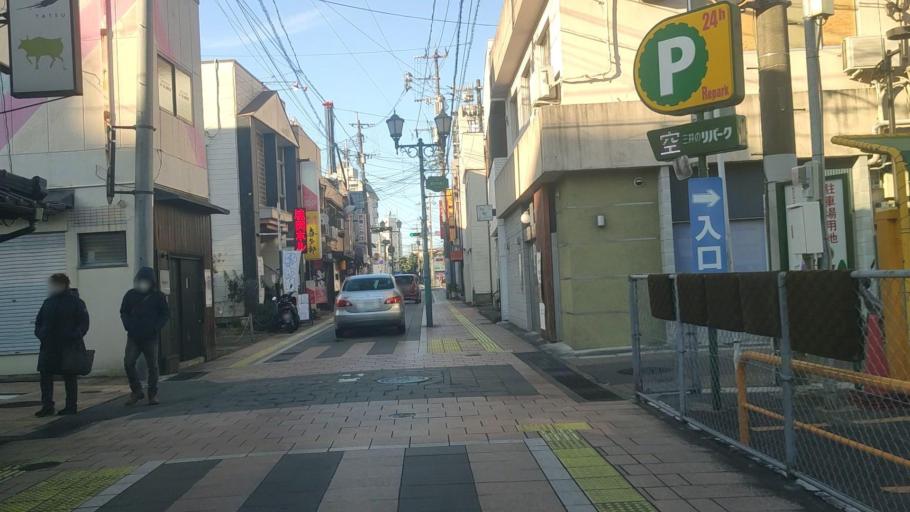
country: JP
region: Oita
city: Beppu
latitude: 33.2782
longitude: 131.5026
